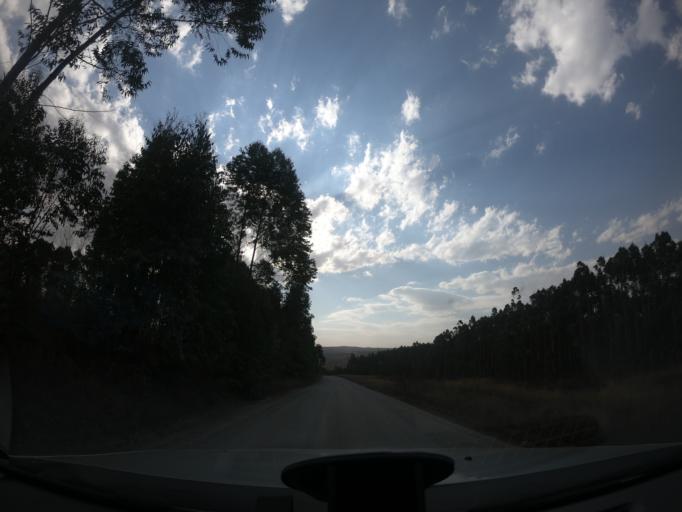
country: ZA
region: KwaZulu-Natal
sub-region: uMgungundlovu District Municipality
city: Howick
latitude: -29.4232
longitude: 30.1046
